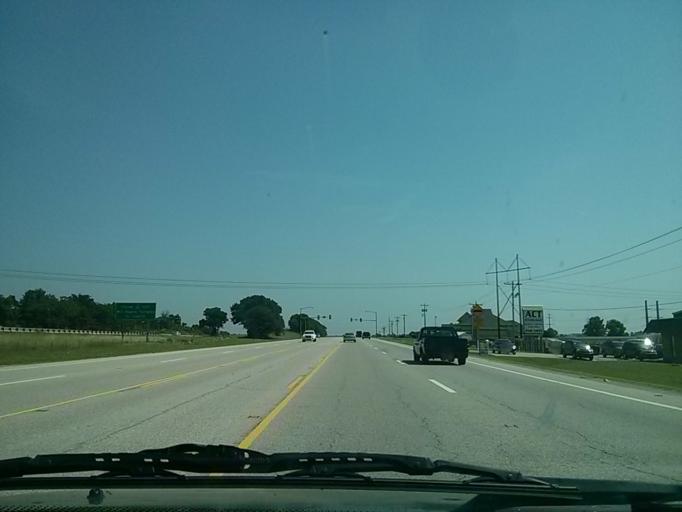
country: US
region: Oklahoma
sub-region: Tulsa County
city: Oakhurst
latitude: 36.0546
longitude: -96.0737
